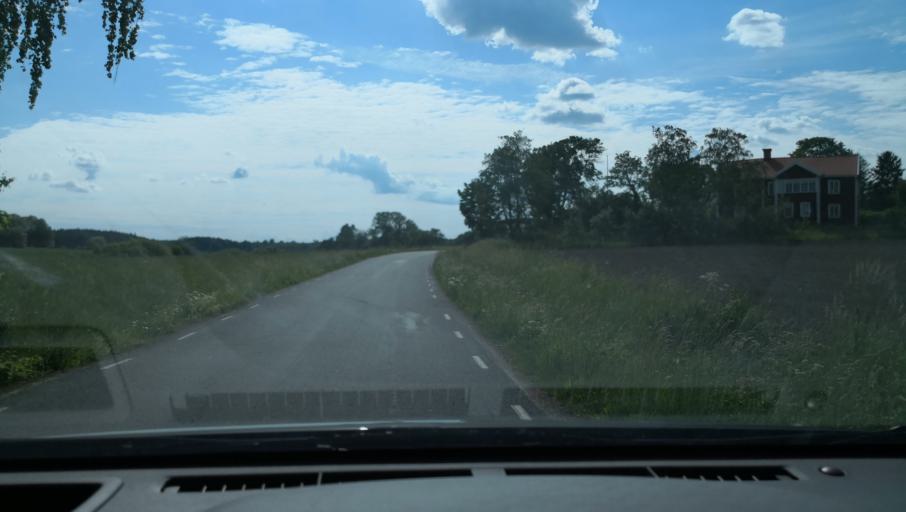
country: SE
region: Uppsala
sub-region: Enkopings Kommun
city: Orsundsbro
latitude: 59.8158
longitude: 17.3464
